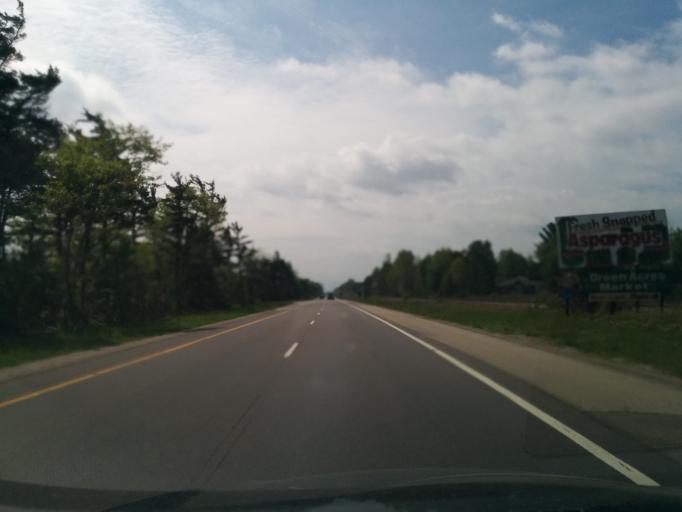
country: US
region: Michigan
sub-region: Ottawa County
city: Grand Haven
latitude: 43.0066
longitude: -86.2046
